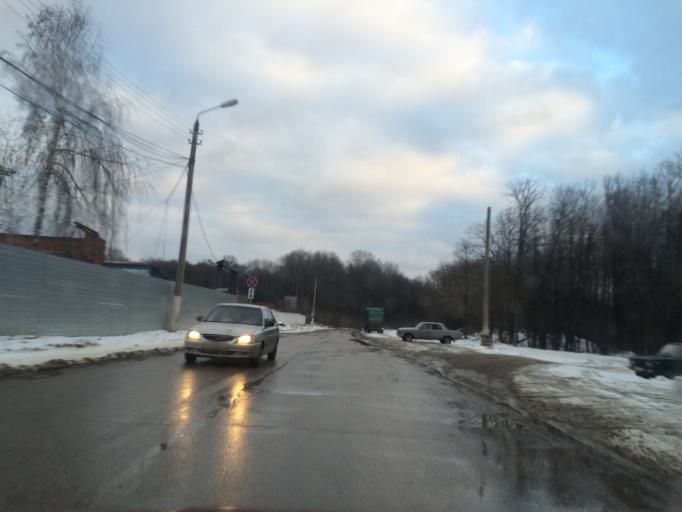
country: RU
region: Tula
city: Tula
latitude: 54.2165
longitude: 37.7133
